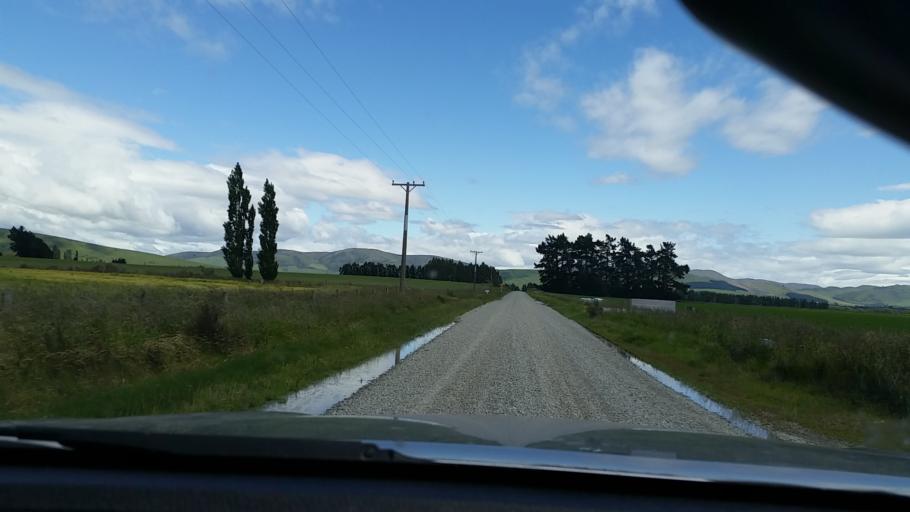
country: NZ
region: Southland
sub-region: Southland District
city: Winton
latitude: -45.7819
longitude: 168.4489
